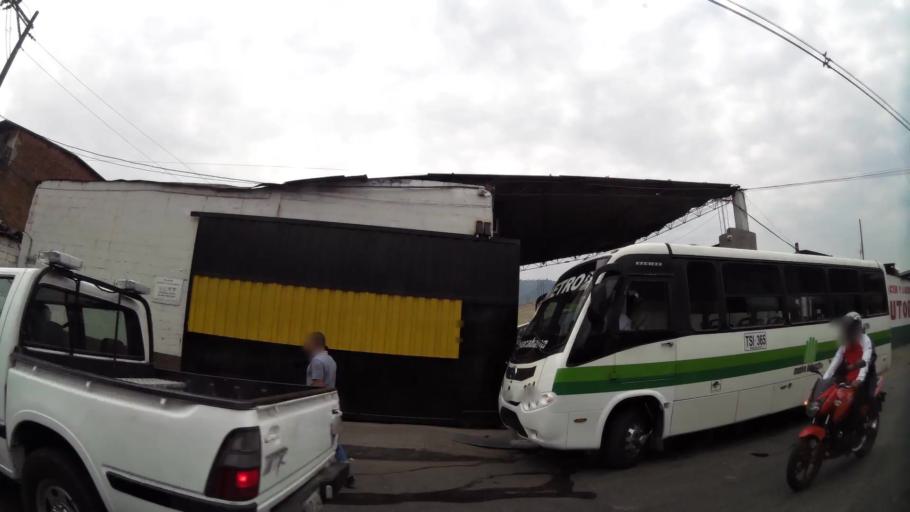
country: CO
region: Antioquia
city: Bello
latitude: 6.3059
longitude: -75.5557
